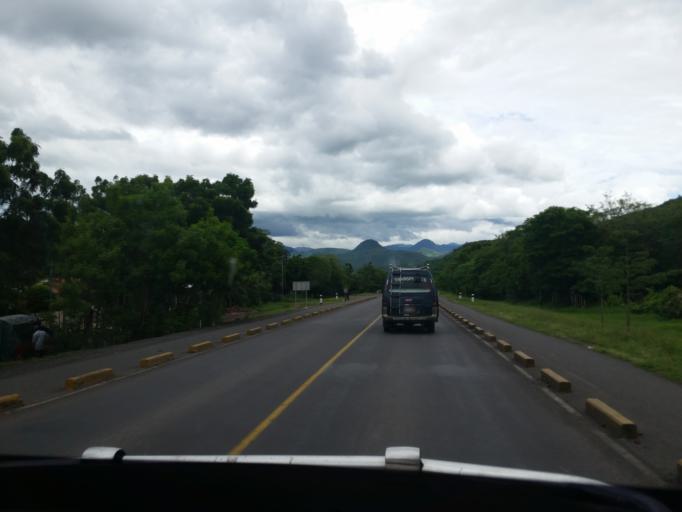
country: NI
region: Matagalpa
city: Ciudad Dario
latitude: 12.8697
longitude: -86.0895
